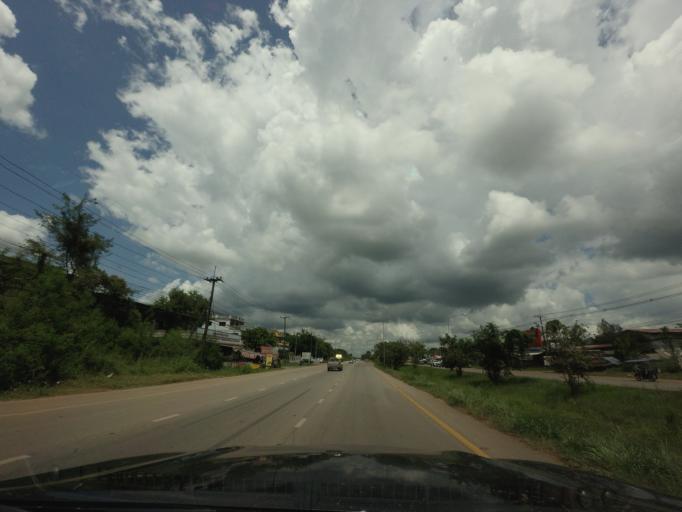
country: TH
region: Changwat Udon Thani
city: Udon Thani
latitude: 17.5346
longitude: 102.7999
